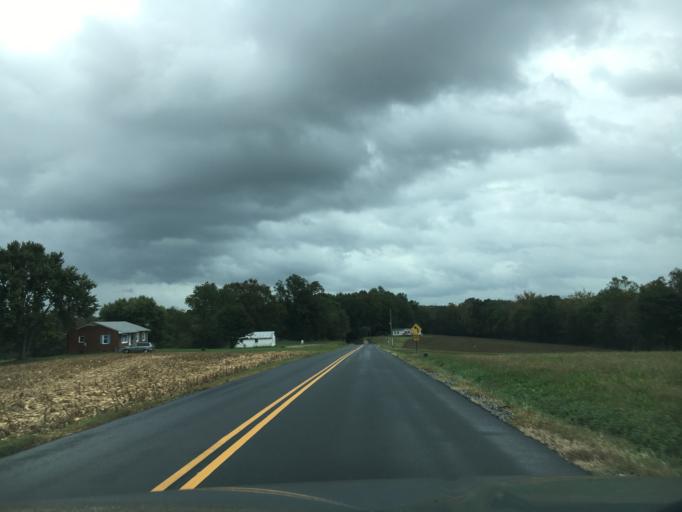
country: US
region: Virginia
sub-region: Amelia County
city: Amelia Court House
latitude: 37.4105
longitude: -77.9626
